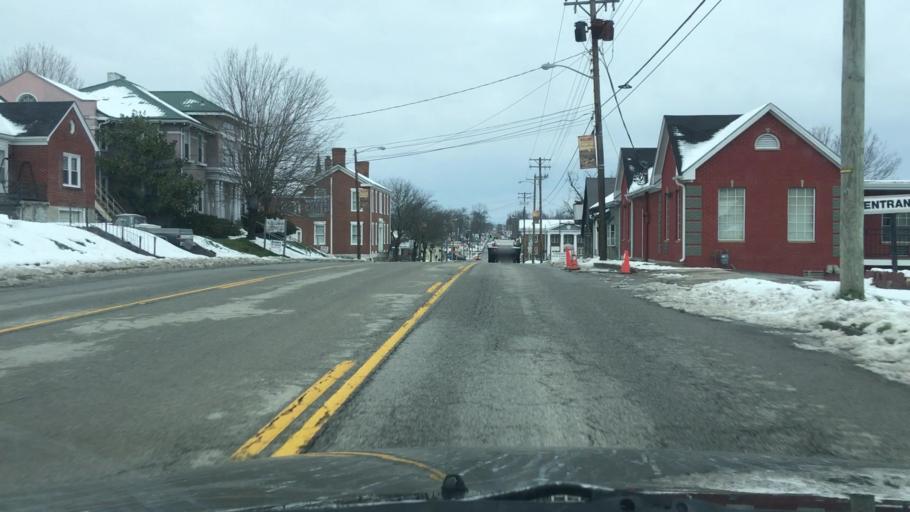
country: US
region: Kentucky
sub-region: Mercer County
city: Harrodsburg
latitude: 37.7606
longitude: -84.8458
